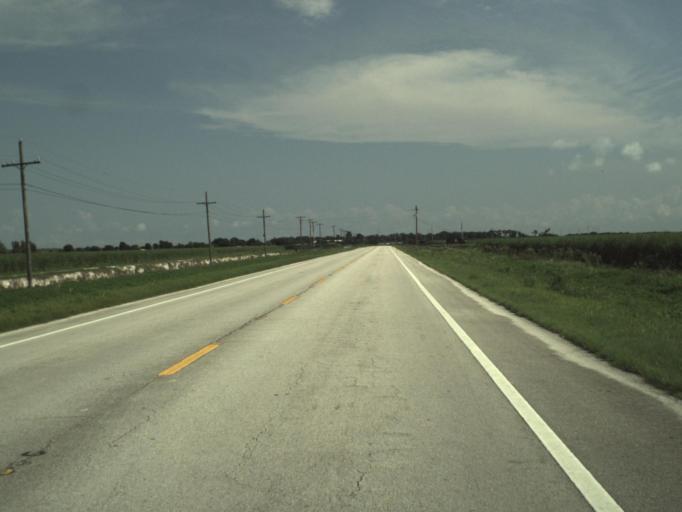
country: US
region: Florida
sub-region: Palm Beach County
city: Belle Glade
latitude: 26.7306
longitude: -80.6841
